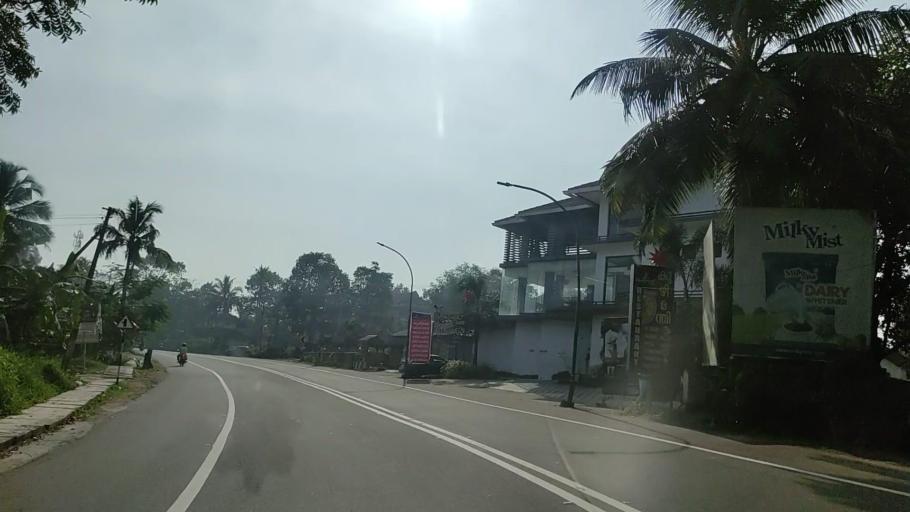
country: IN
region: Kerala
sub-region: Kollam
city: Punalur
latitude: 8.9794
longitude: 76.8113
